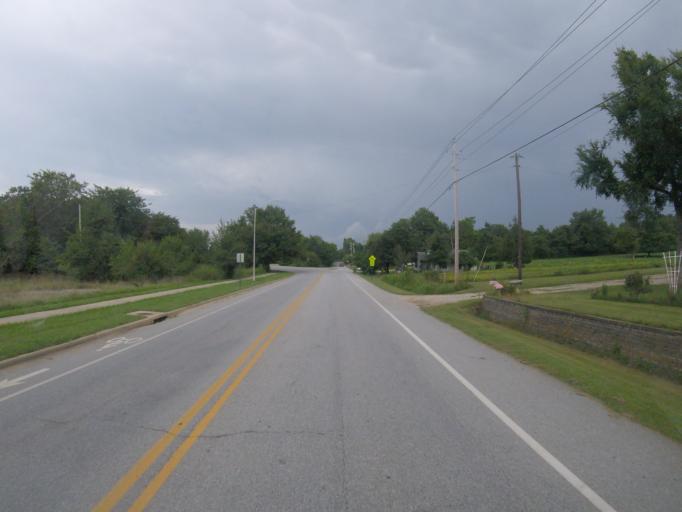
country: US
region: Arkansas
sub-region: Washington County
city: Fayetteville
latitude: 36.0452
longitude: -94.1869
